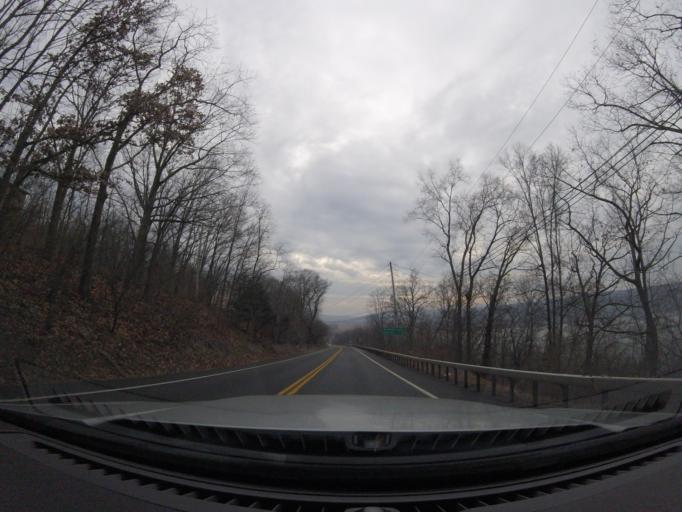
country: US
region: New York
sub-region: Schuyler County
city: Watkins Glen
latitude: 42.3975
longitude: -76.8576
